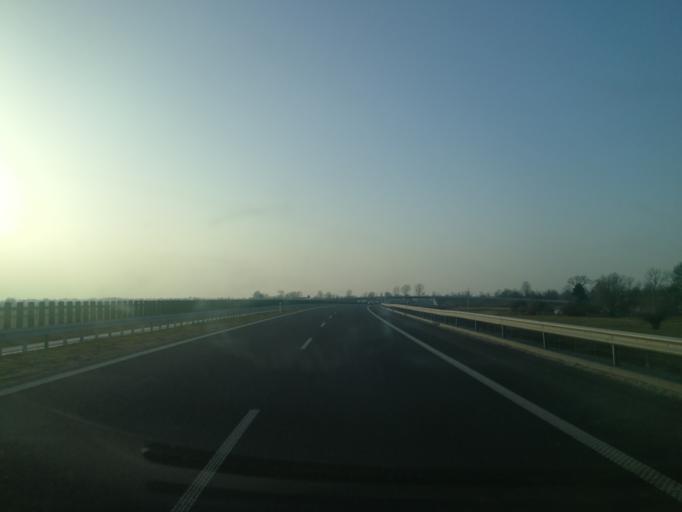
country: PL
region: Pomeranian Voivodeship
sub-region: Powiat nowodworski
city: Nowy Dwor Gdanski
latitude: 54.1743
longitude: 19.1971
